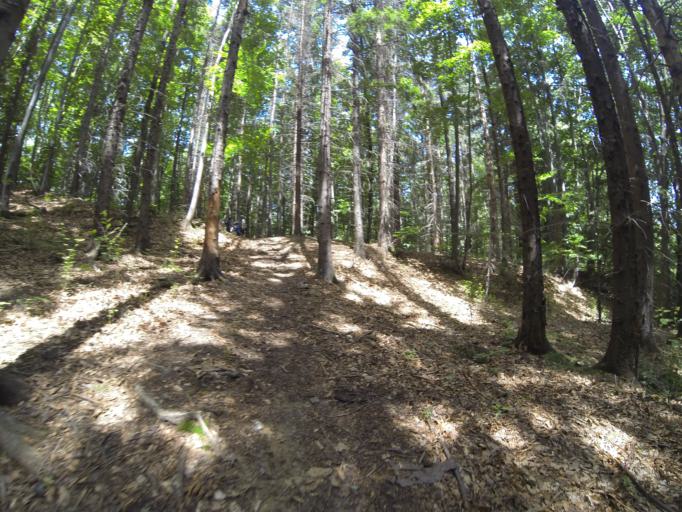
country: RO
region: Valcea
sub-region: Oras Baile Olanesti
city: Baile Olanesti
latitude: 45.2163
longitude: 24.2000
